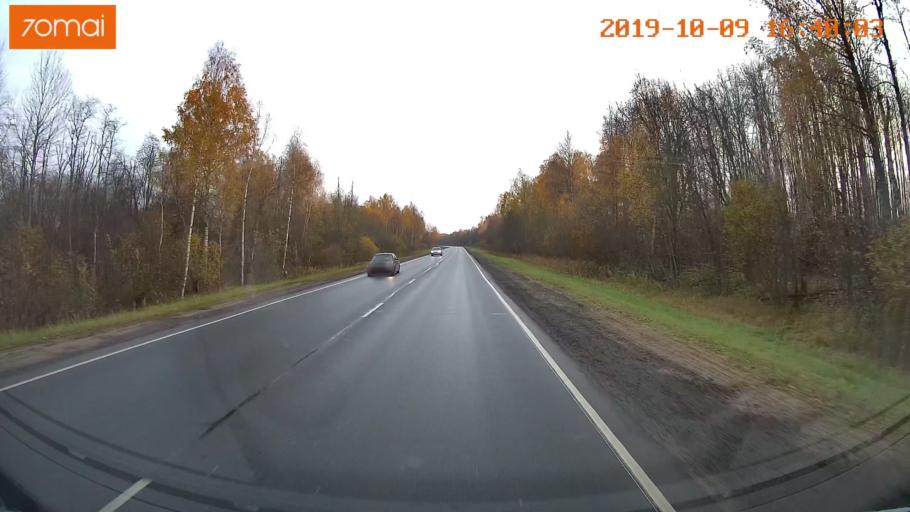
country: RU
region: Kostroma
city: Volgorechensk
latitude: 57.4892
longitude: 41.0558
